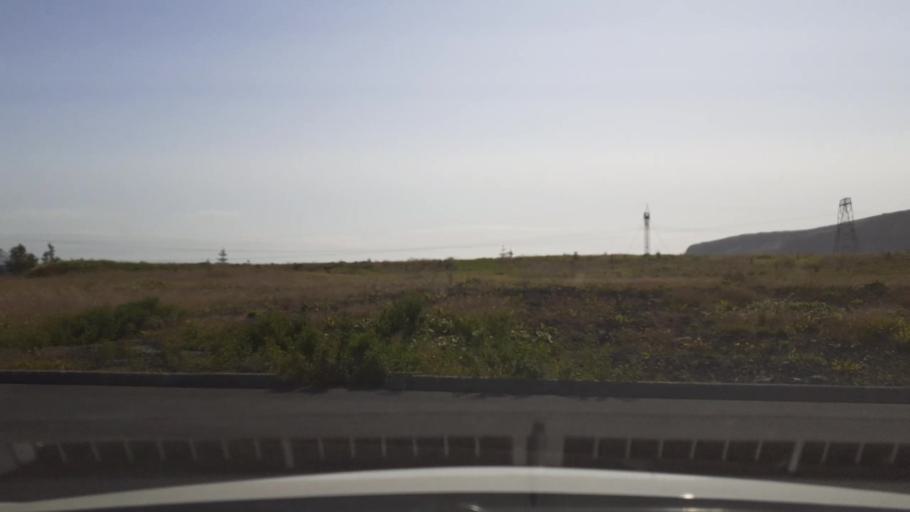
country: IS
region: South
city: Hveragerdi
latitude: 63.9994
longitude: -21.2055
